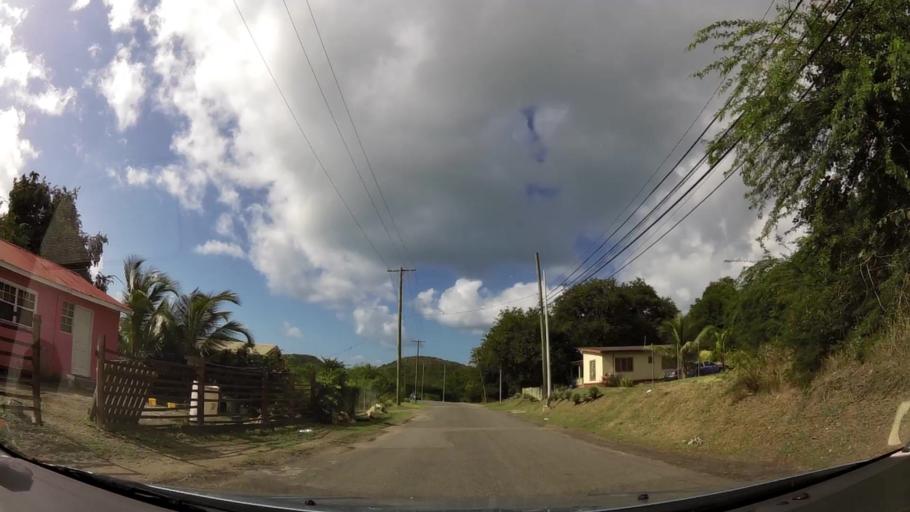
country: AG
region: Saint John
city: Saint John's
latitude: 17.1167
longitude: -61.8633
